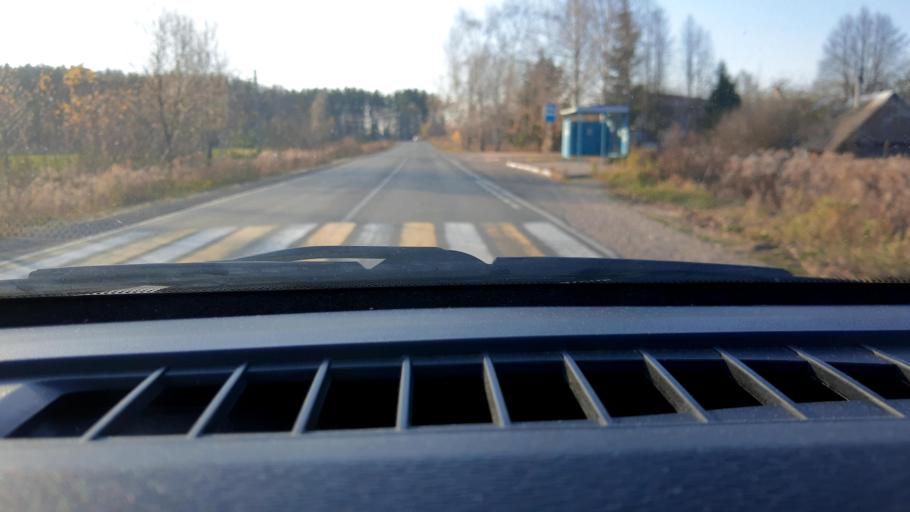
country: RU
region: Nizjnij Novgorod
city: Neklyudovo
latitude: 56.4483
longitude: 43.8998
